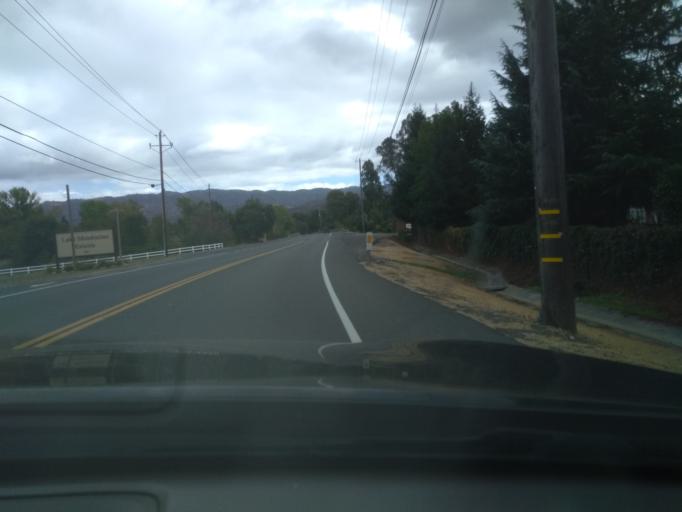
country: US
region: California
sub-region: Mendocino County
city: Ukiah
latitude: 39.1956
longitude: -123.1975
